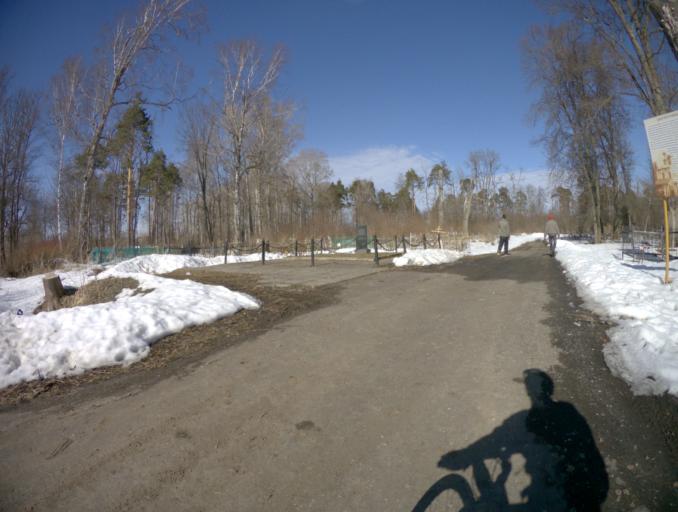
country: RU
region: Vladimir
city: Suzdal'
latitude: 56.4297
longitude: 40.4600
